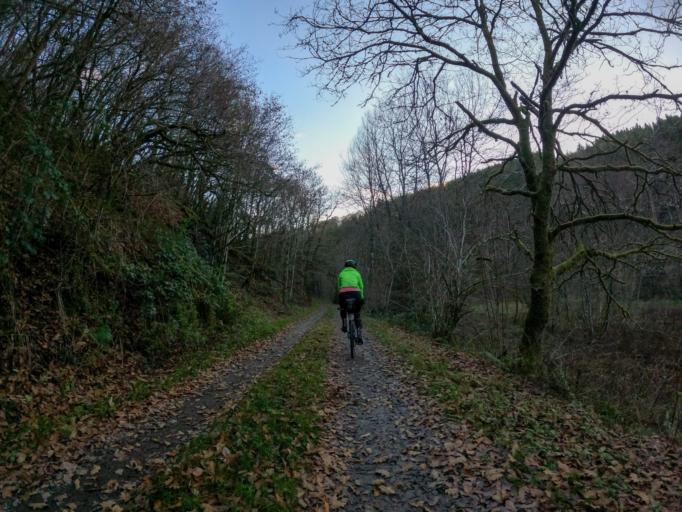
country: LU
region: Diekirch
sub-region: Canton de Wiltz
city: Bavigne
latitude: 49.9427
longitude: 5.8332
